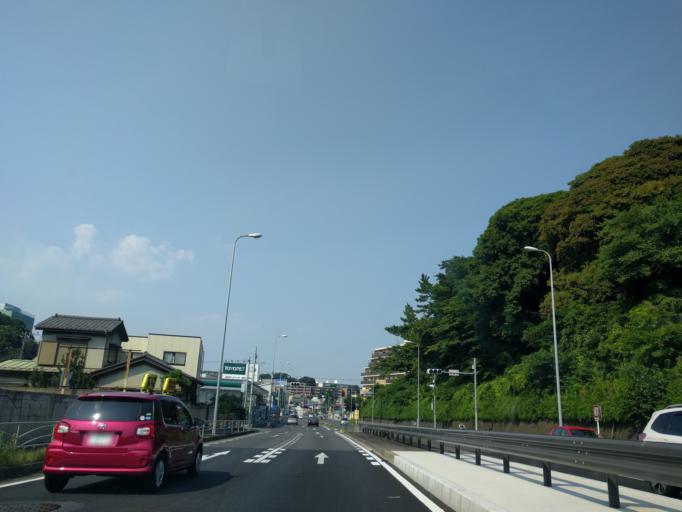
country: JP
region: Kanagawa
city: Yokohama
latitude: 35.4953
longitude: 139.6594
